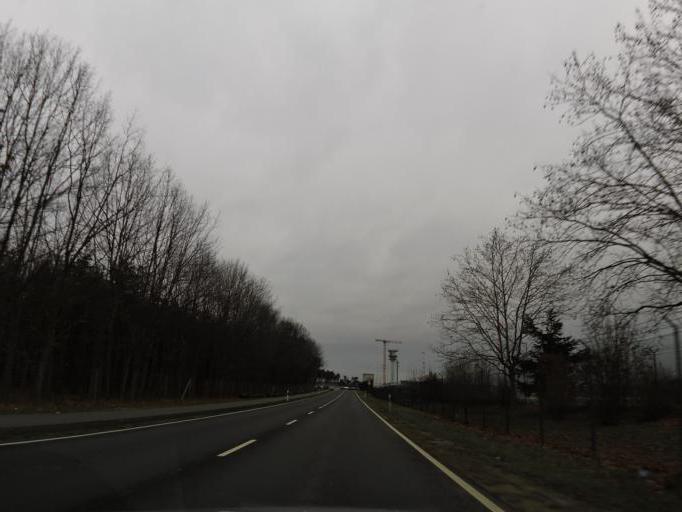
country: DE
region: Hesse
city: Kelsterbach
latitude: 50.0309
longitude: 8.5201
